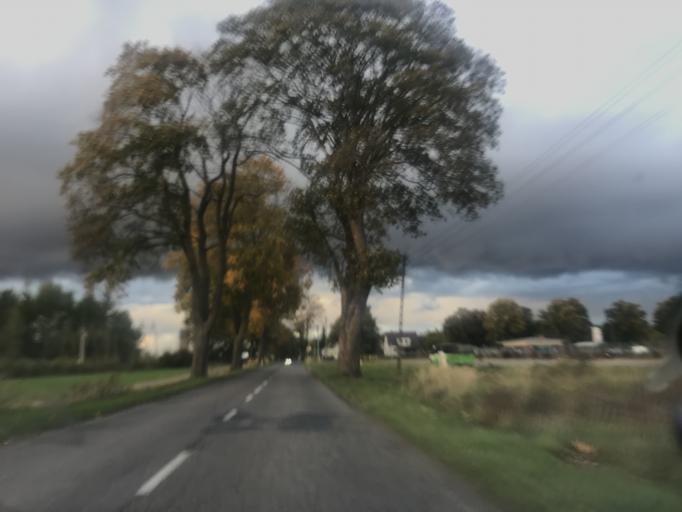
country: PL
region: West Pomeranian Voivodeship
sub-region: Powiat walecki
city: Tuczno
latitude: 53.2154
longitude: 16.1707
